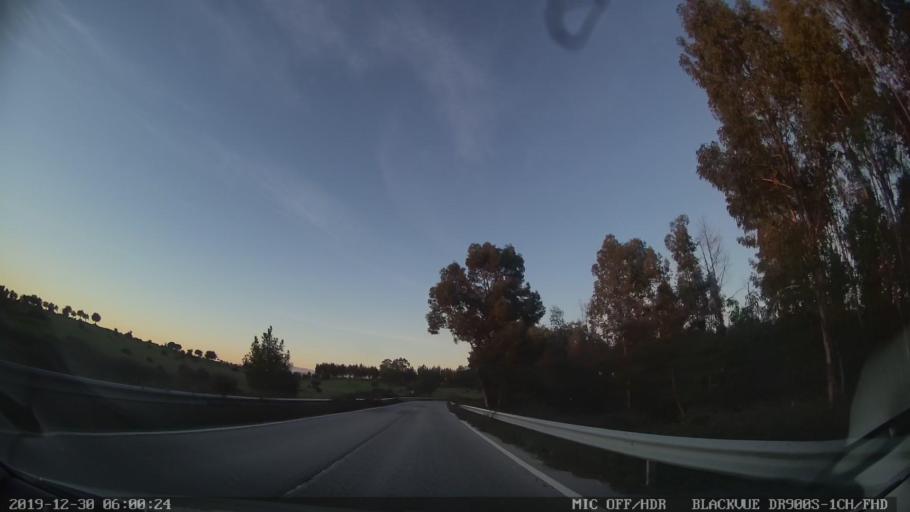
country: PT
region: Castelo Branco
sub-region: Idanha-A-Nova
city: Idanha-a-Nova
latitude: 40.0521
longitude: -7.2456
